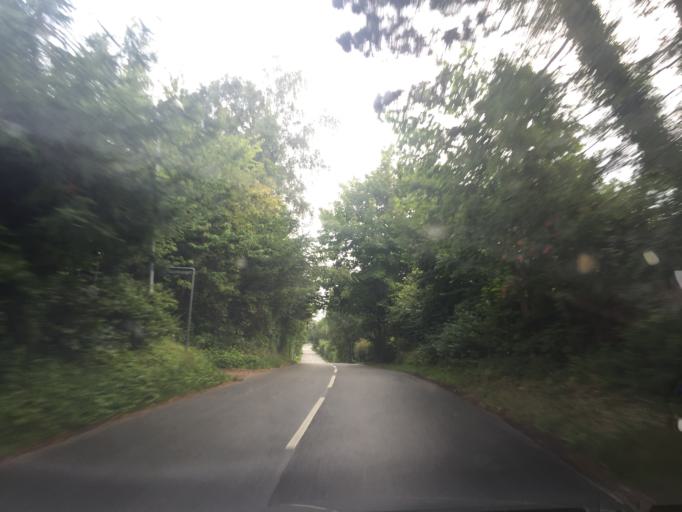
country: DK
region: Capital Region
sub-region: Halsnaes Kommune
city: Liseleje
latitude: 56.0029
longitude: 11.9675
